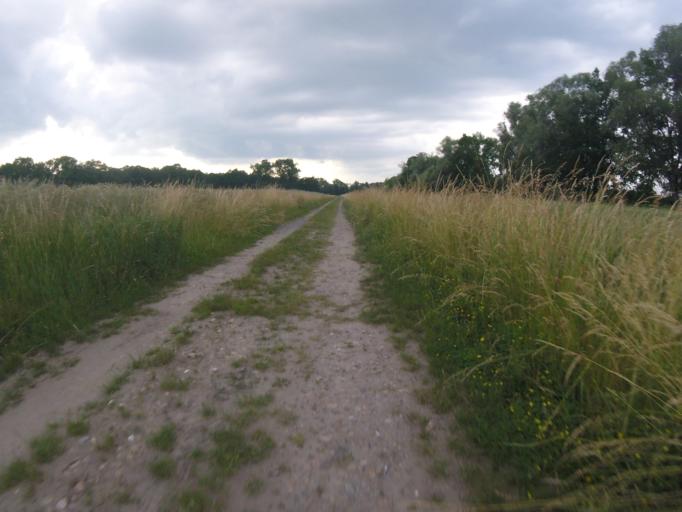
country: DE
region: Brandenburg
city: Konigs Wusterhausen
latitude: 52.2810
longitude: 13.5868
